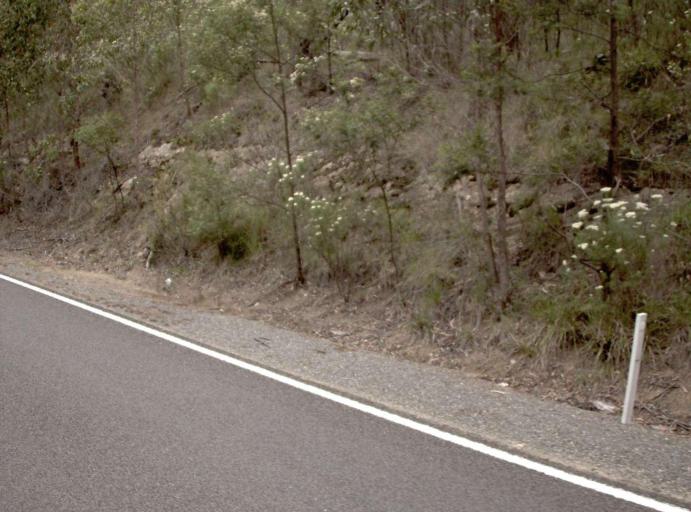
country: AU
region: New South Wales
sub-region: Bombala
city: Bombala
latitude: -37.2719
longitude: 149.2272
